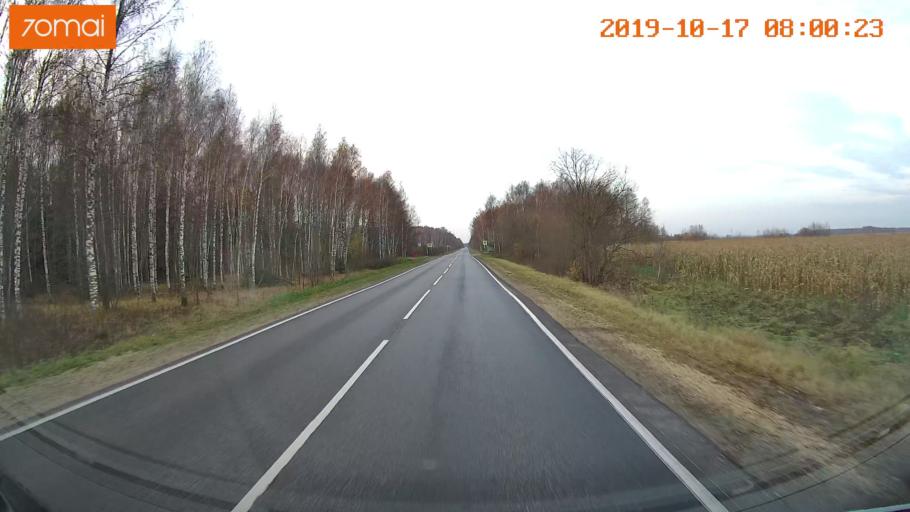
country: RU
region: Vladimir
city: Bavleny
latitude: 56.3840
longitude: 39.5192
